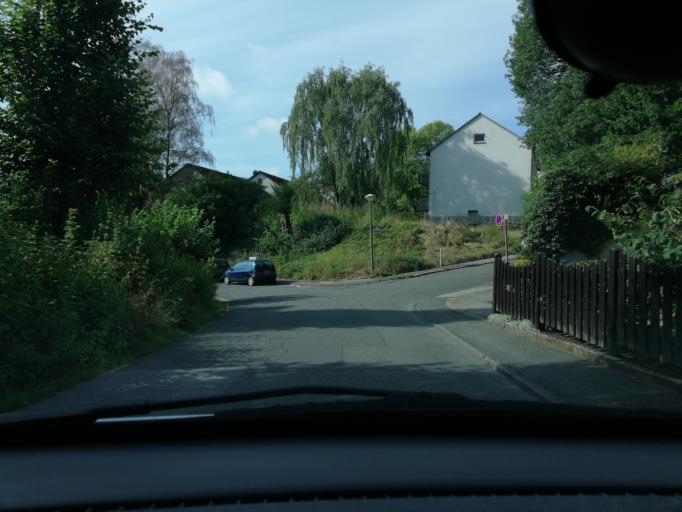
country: DE
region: North Rhine-Westphalia
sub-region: Regierungsbezirk Arnsberg
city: Schwelm
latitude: 51.3133
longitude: 7.2892
